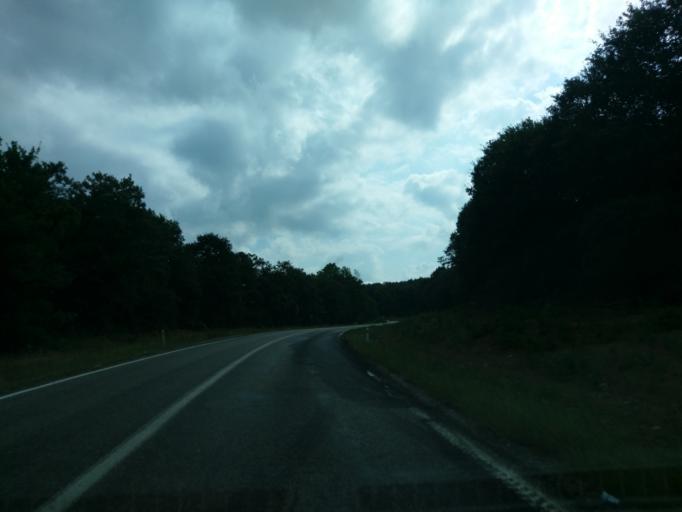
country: TR
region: Sinop
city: Yenikonak
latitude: 41.9447
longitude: 34.7375
